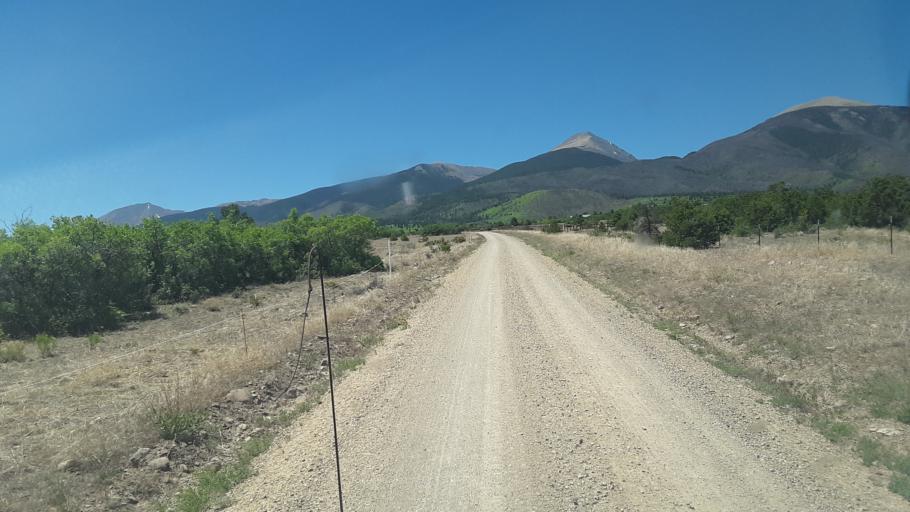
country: US
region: Colorado
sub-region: Custer County
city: Westcliffe
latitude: 38.2987
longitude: -105.6699
